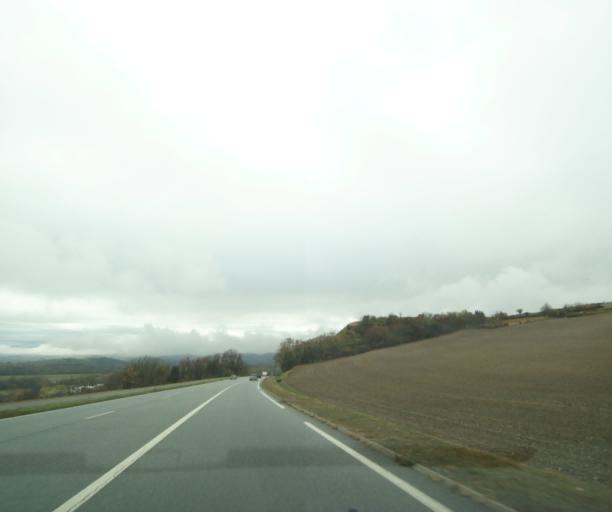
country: FR
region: Auvergne
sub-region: Departement du Puy-de-Dome
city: Cournon-d'Auvergne
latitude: 45.7582
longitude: 3.2101
